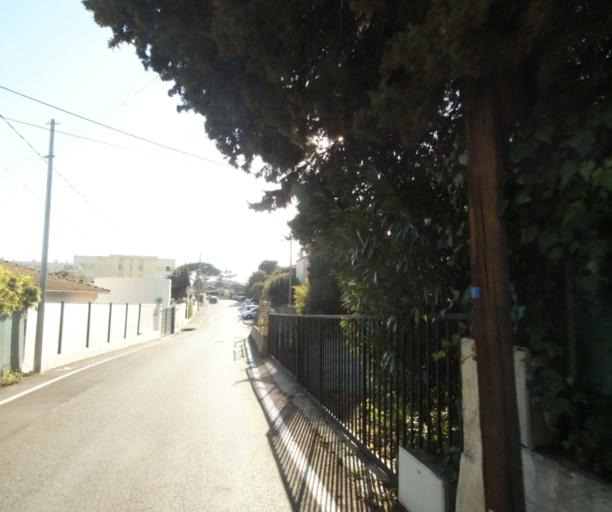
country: FR
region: Provence-Alpes-Cote d'Azur
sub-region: Departement des Alpes-Maritimes
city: Biot
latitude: 43.6075
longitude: 7.1215
